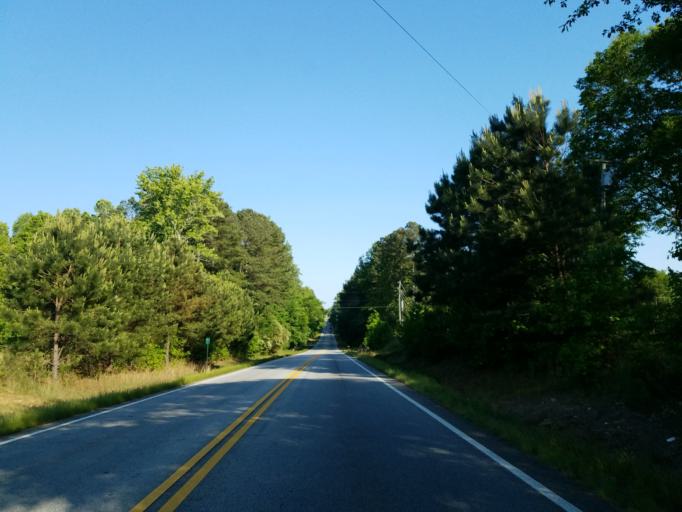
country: US
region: Georgia
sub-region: Carroll County
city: Villa Rica
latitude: 33.7595
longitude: -84.9430
